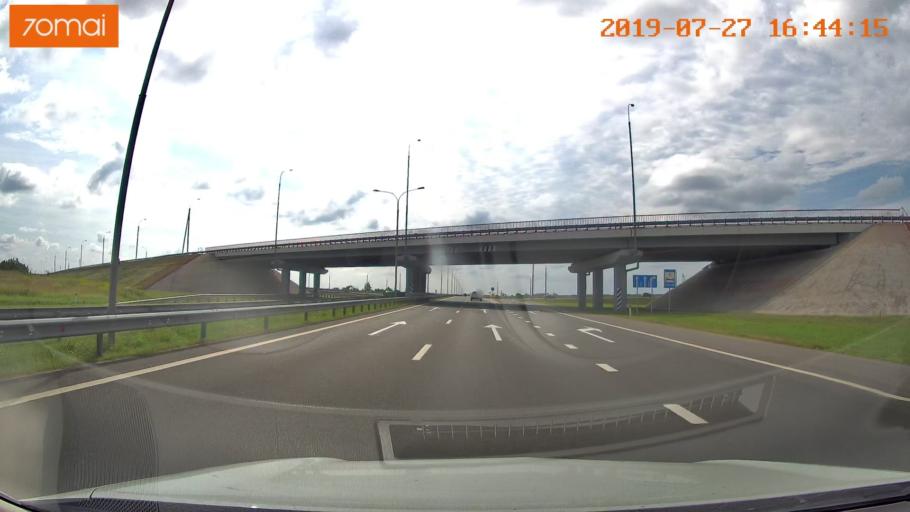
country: RU
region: Kaliningrad
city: Gvardeysk
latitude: 54.6726
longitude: 21.0817
